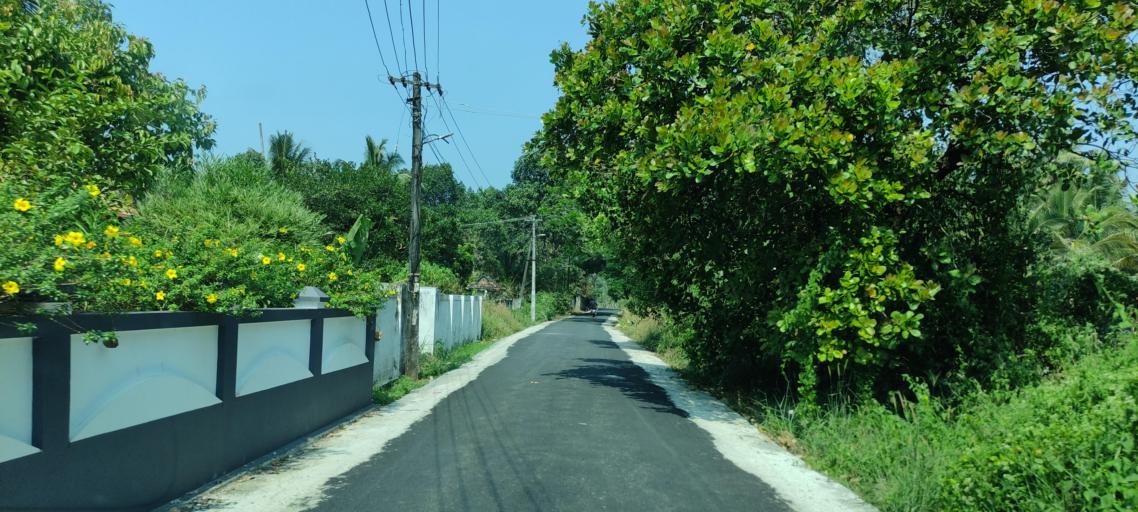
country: IN
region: Kerala
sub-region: Alappuzha
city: Alleppey
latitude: 9.5373
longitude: 76.3209
